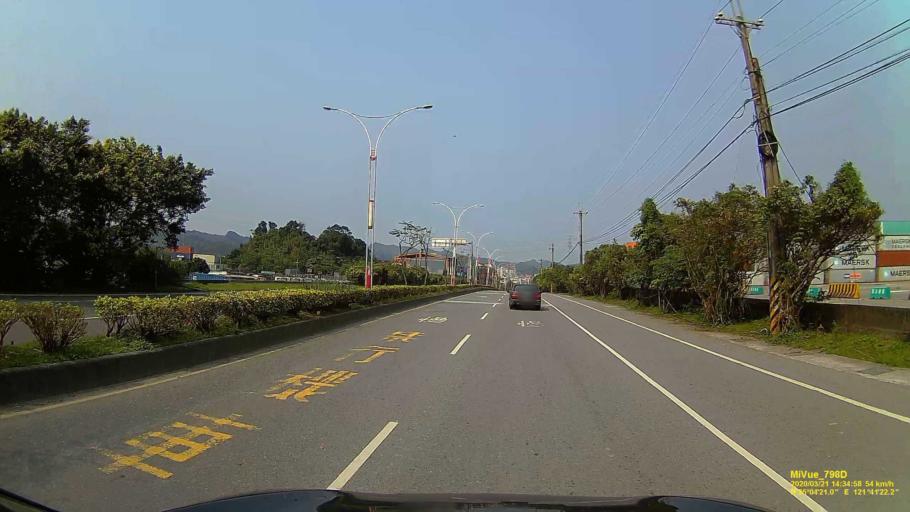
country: TW
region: Taiwan
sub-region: Keelung
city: Keelung
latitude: 25.0727
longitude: 121.6896
